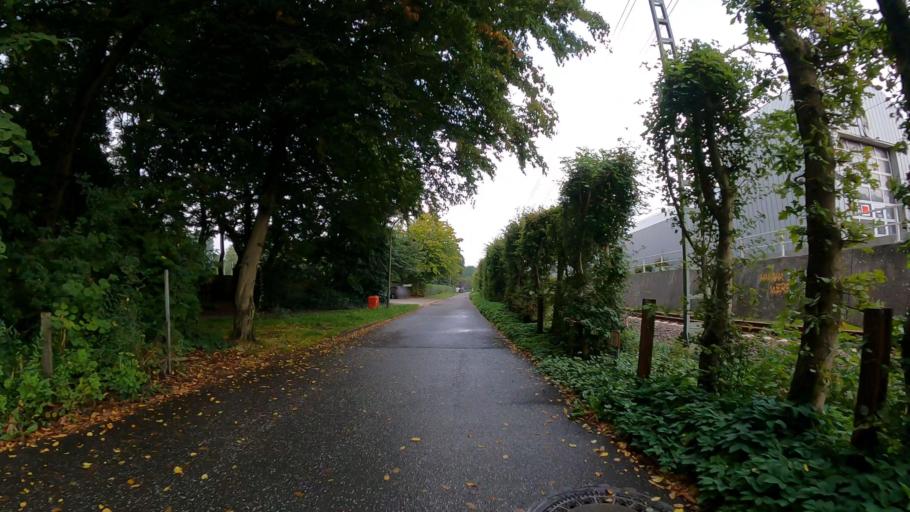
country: DE
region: Hamburg
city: Eidelstedt
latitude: 53.6077
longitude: 9.8780
